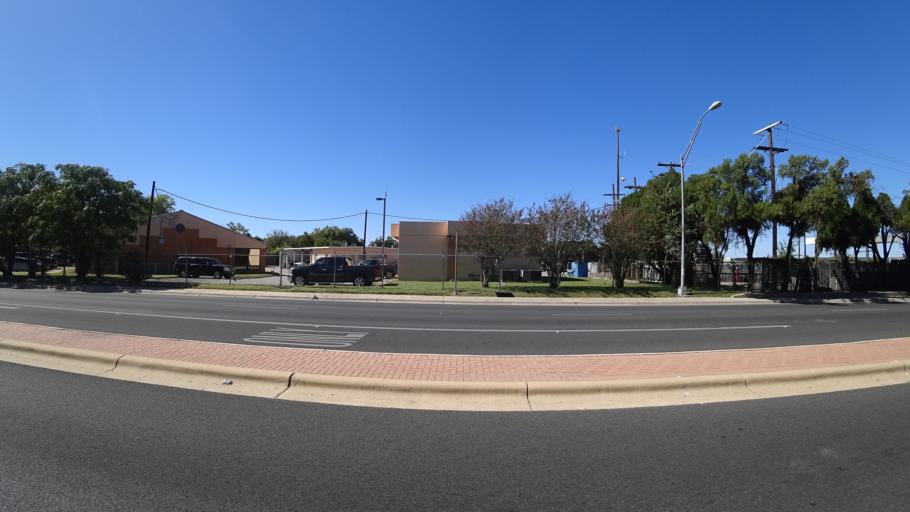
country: US
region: Texas
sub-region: Travis County
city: Austin
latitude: 30.3271
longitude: -97.7272
